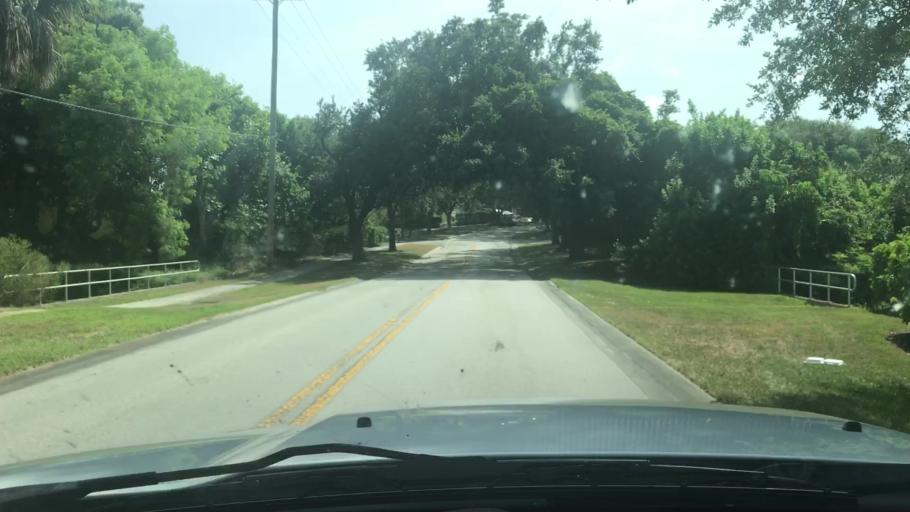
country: US
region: Florida
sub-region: Indian River County
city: Florida Ridge
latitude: 27.5650
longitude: -80.3779
